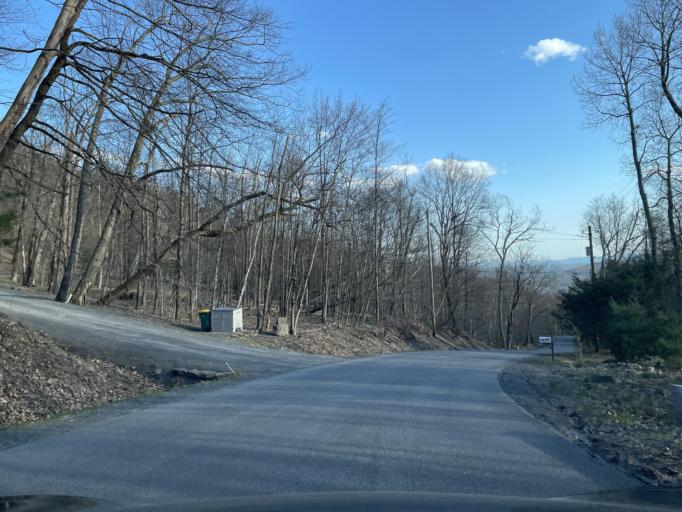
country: US
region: New York
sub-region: Ulster County
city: Woodstock
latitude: 42.0687
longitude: -74.1223
